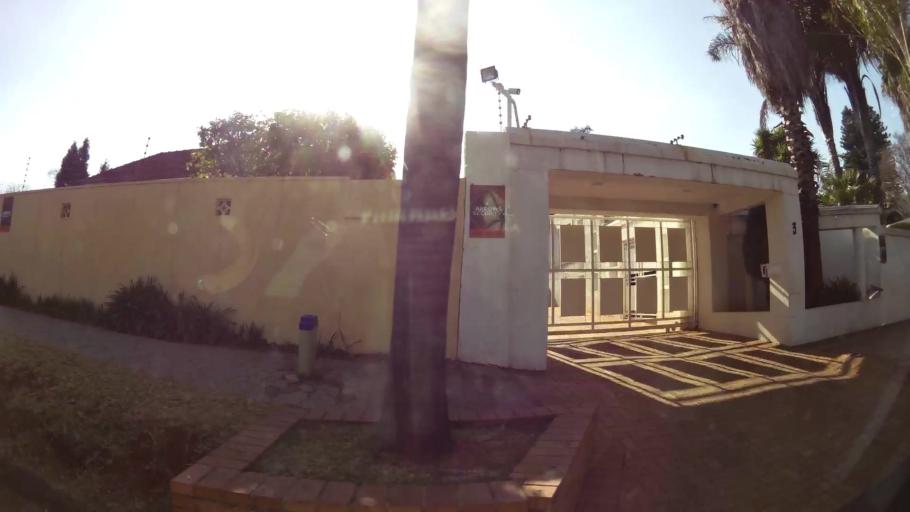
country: ZA
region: Gauteng
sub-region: City of Johannesburg Metropolitan Municipality
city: Johannesburg
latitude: -26.1764
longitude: 28.1042
